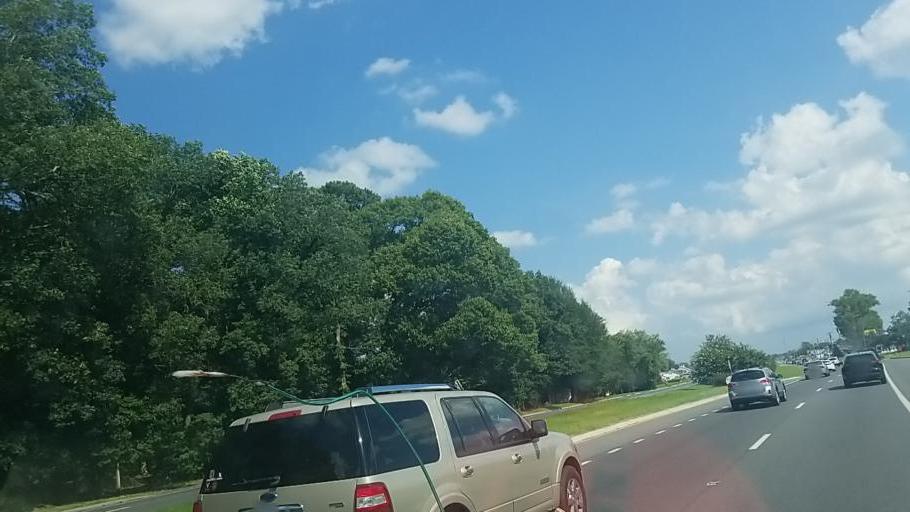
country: US
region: Delaware
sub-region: Sussex County
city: Millsboro
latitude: 38.5935
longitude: -75.3096
